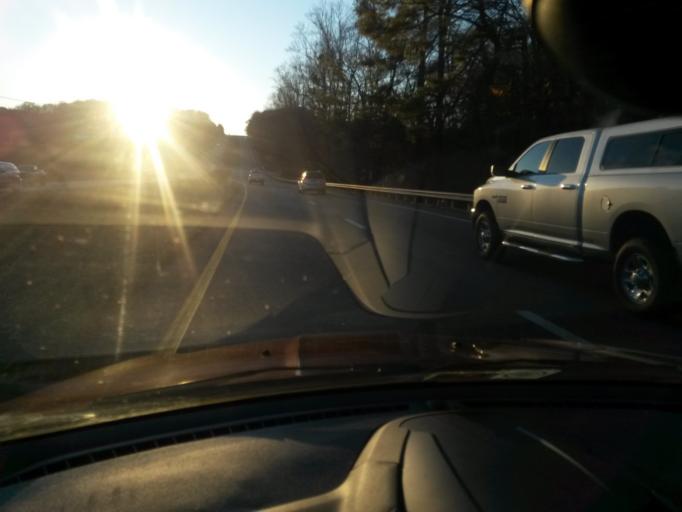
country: US
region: Virginia
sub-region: Franklin County
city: Rocky Mount
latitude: 37.0897
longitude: -79.9353
